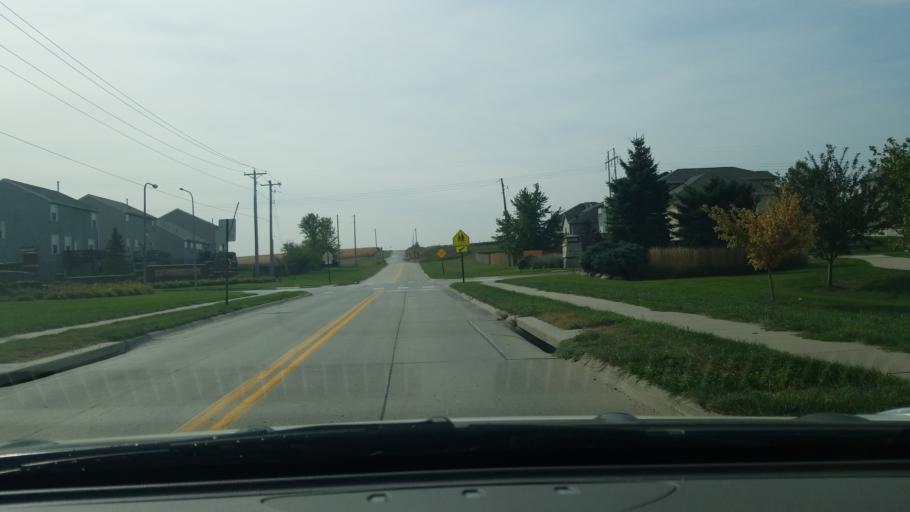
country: US
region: Nebraska
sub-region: Sarpy County
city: Papillion
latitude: 41.1269
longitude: -96.0621
